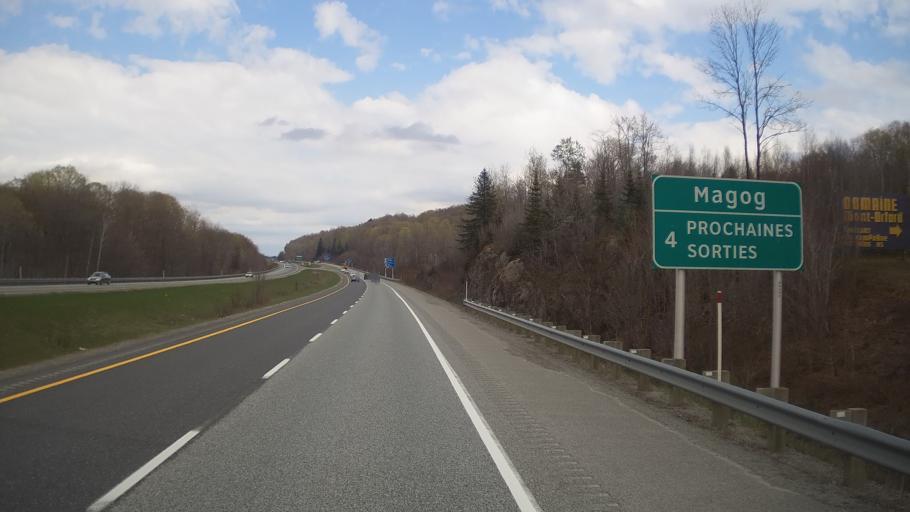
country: CA
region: Quebec
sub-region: Estrie
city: Magog
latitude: 45.2892
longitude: -72.2553
